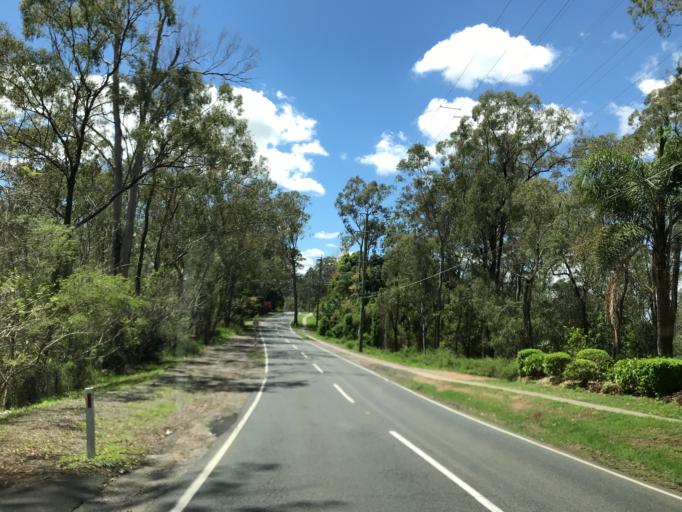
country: AU
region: Queensland
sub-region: Brisbane
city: Kenmore Hills
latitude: -27.5231
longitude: 152.9439
